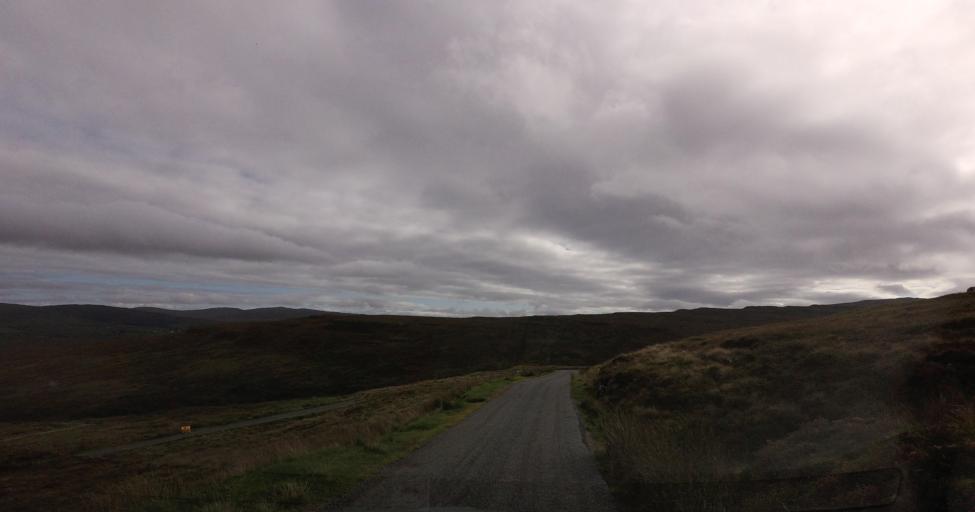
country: GB
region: Scotland
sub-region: Highland
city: Isle of Skye
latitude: 57.4119
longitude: -6.2609
